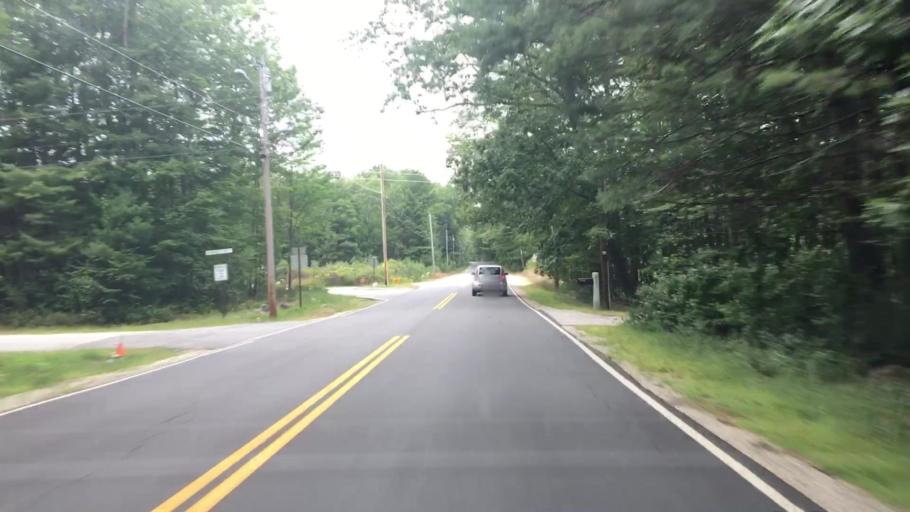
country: US
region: Maine
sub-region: Cumberland County
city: Cumberland Center
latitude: 43.8826
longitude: -70.2486
